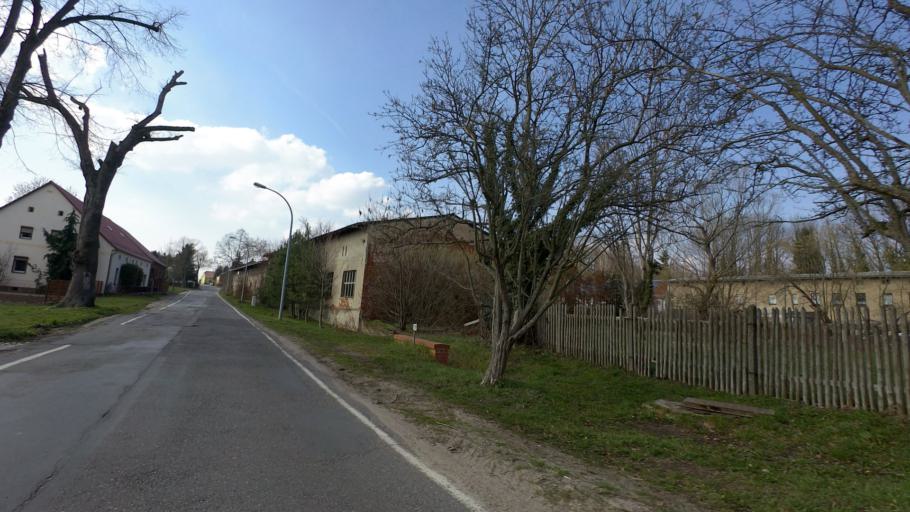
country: DE
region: Brandenburg
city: Ihlow
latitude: 51.9526
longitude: 13.3647
